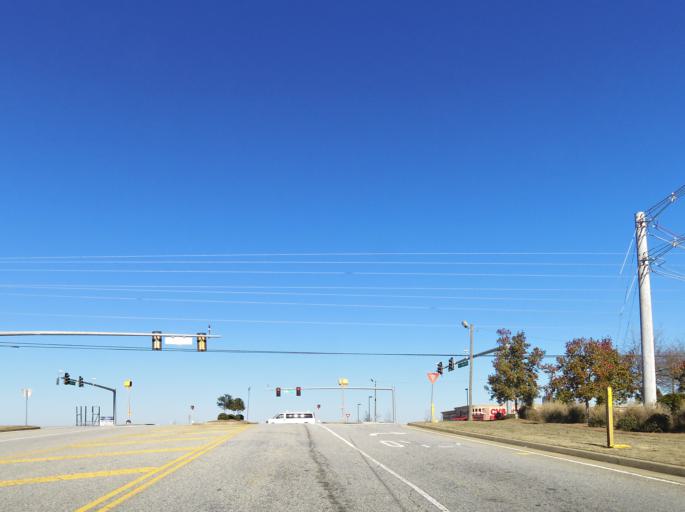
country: US
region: Georgia
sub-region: Peach County
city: Byron
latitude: 32.7435
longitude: -83.7227
